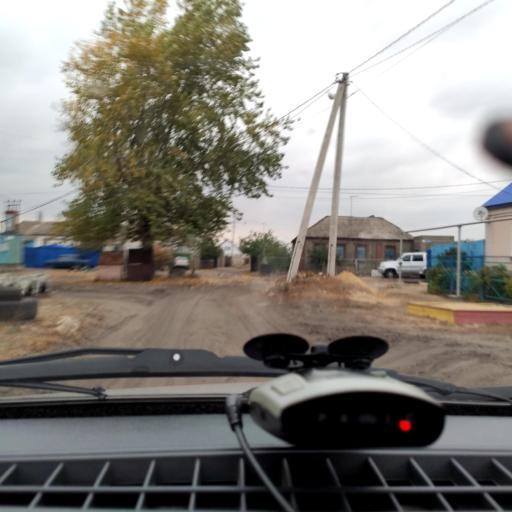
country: RU
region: Voronezj
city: Pridonskoy
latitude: 51.7037
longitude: 39.0691
